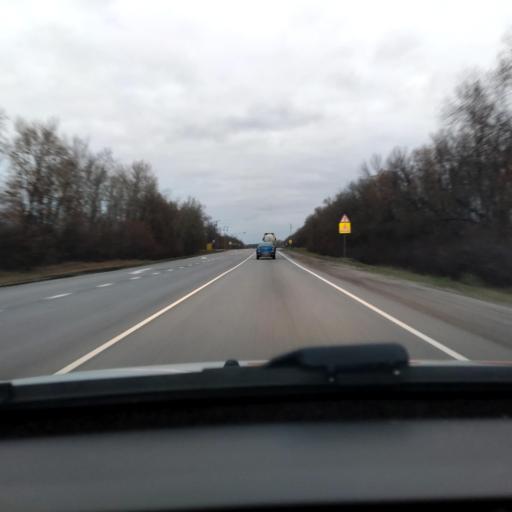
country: RU
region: Lipetsk
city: Borinskoye
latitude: 52.4166
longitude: 39.2517
